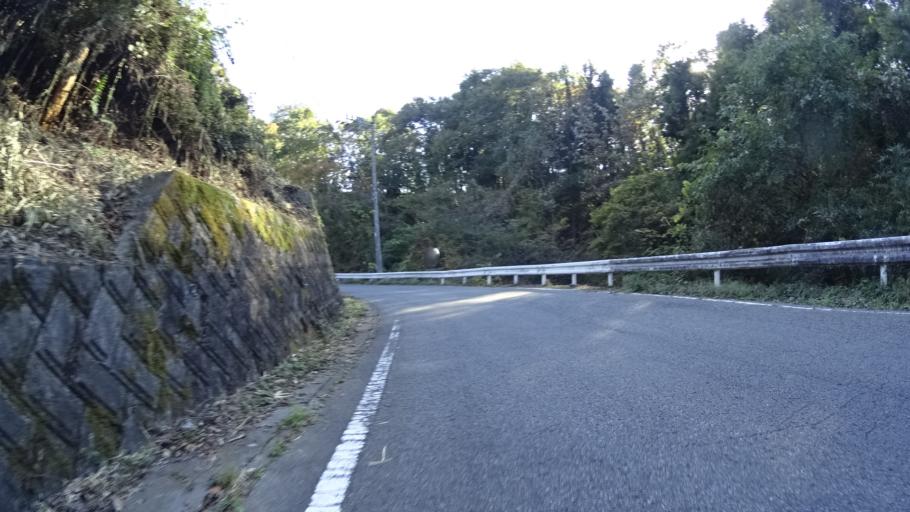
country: JP
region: Yamanashi
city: Uenohara
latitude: 35.6711
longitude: 139.0964
